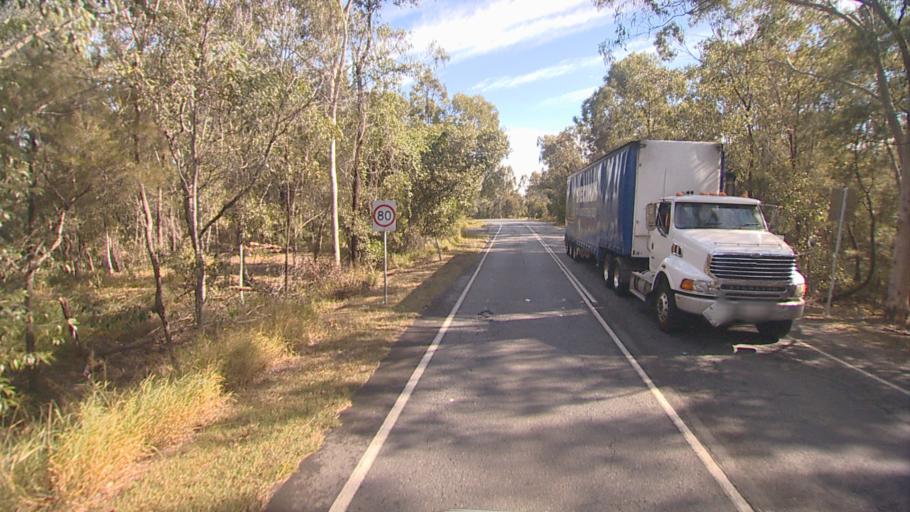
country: AU
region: Queensland
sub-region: Brisbane
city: Forest Lake
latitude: -27.6299
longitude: 152.9453
